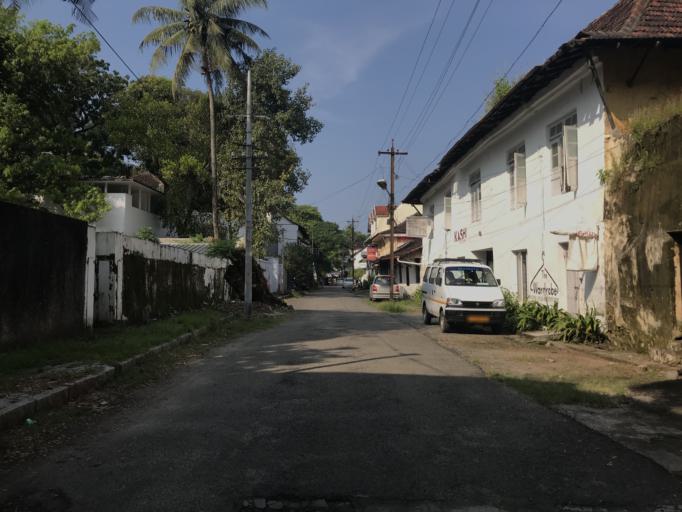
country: IN
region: Kerala
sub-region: Ernakulam
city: Cochin
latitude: 9.9645
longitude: 76.2413
